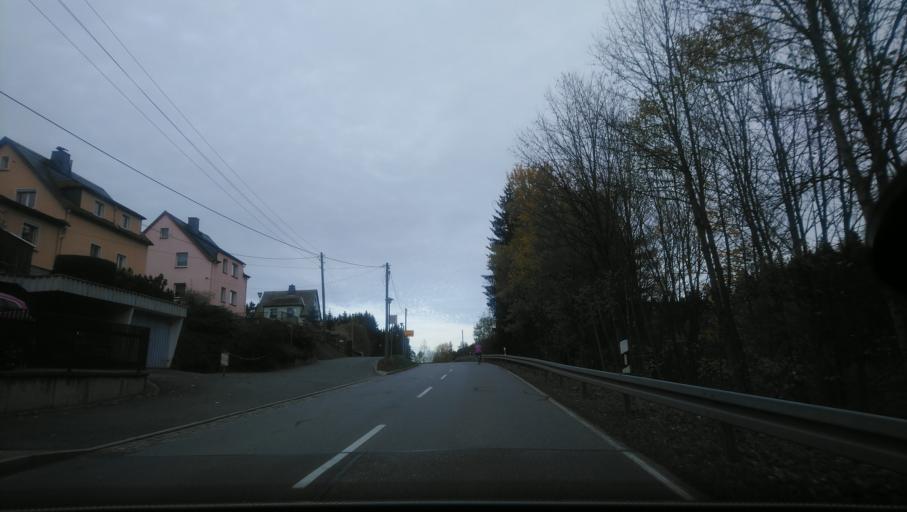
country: DE
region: Saxony
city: Dorfchemnitz
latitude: 50.6748
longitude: 12.8415
